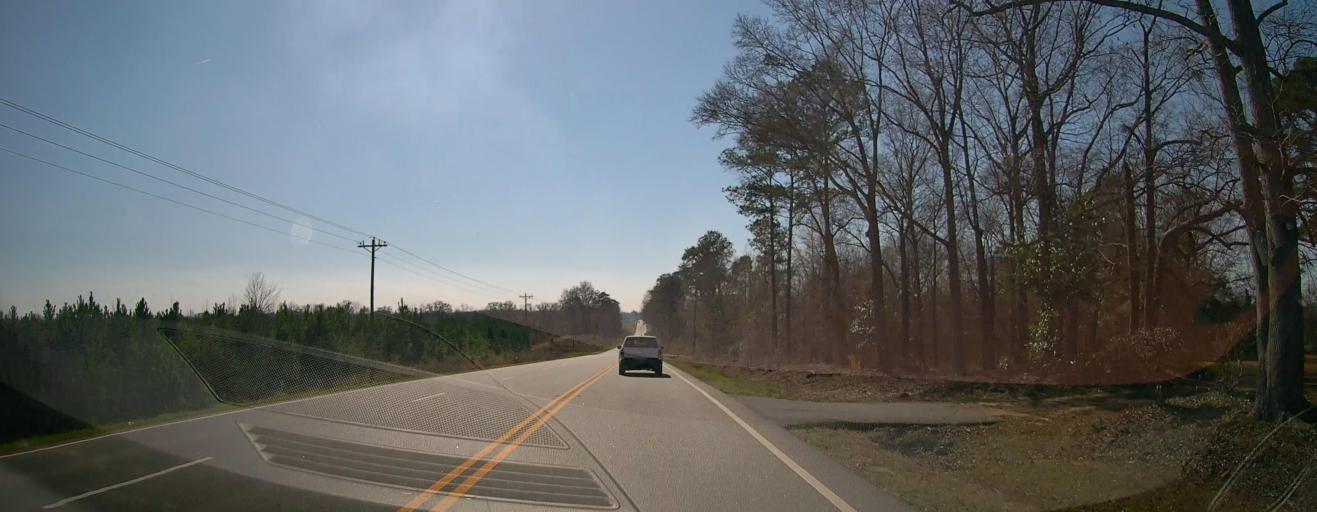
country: US
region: Georgia
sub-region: Macon County
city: Marshallville
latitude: 32.3281
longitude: -83.8728
